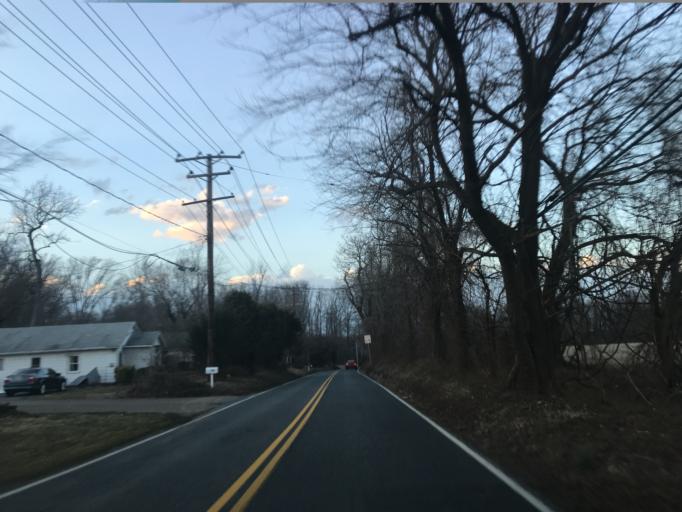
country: US
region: Maryland
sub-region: Harford County
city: Bel Air South
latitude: 39.5447
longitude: -76.2875
